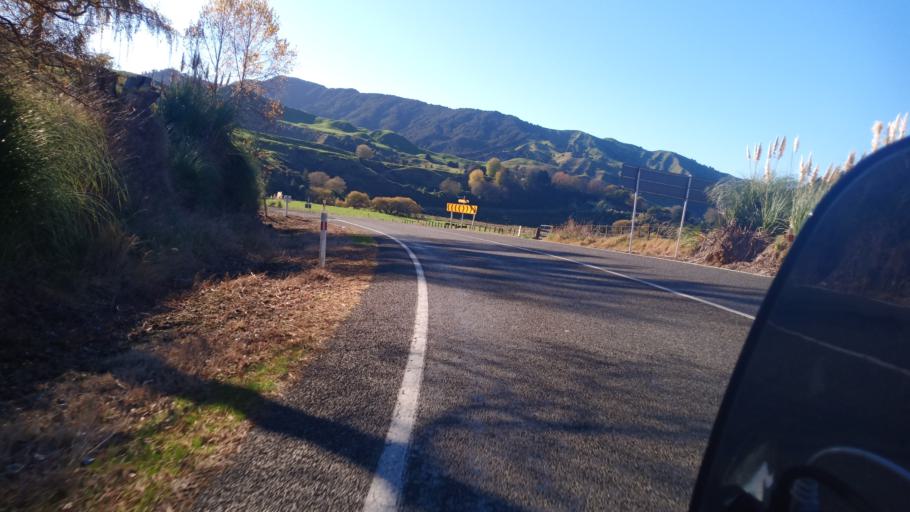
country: NZ
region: Hawke's Bay
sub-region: Wairoa District
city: Wairoa
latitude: -38.8788
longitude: 177.2368
